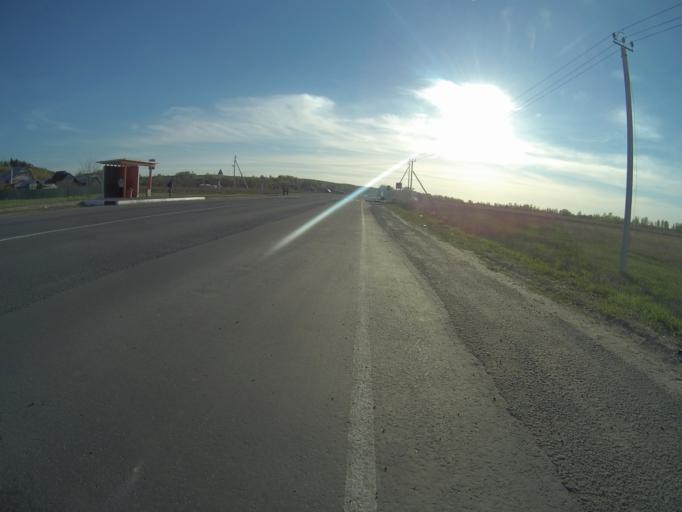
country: RU
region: Vladimir
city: Raduzhnyy
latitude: 56.0232
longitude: 40.3311
